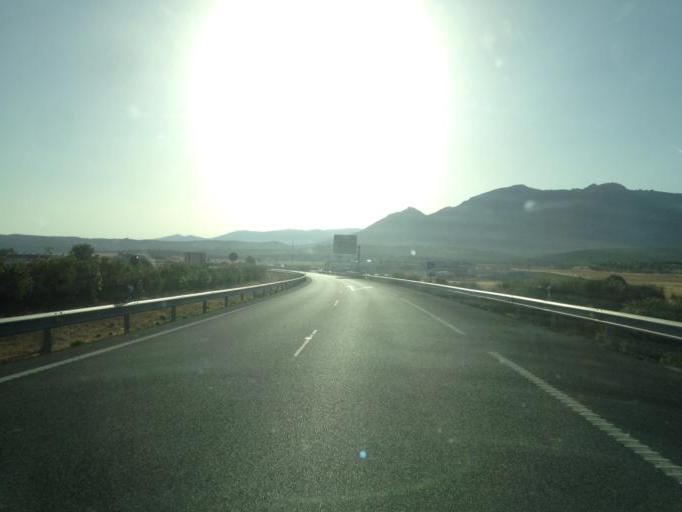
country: ES
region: Andalusia
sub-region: Provincia de Malaga
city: Villanueva del Trabuco
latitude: 37.0661
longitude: -4.3345
